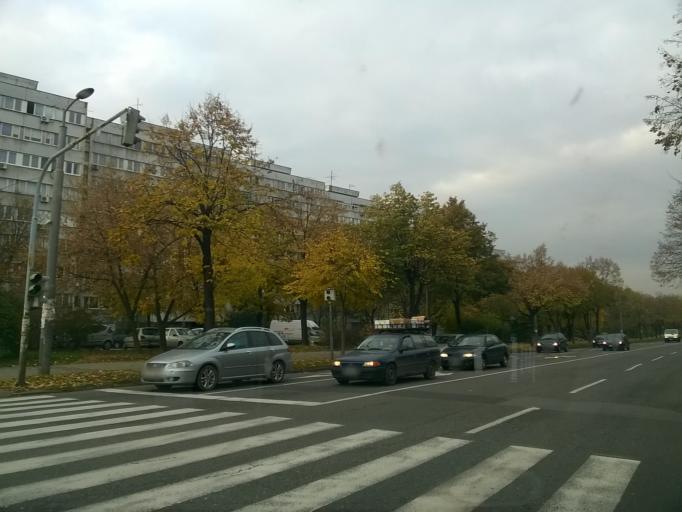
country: RS
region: Central Serbia
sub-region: Belgrade
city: Vozdovac
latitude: 44.7841
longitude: 20.4911
